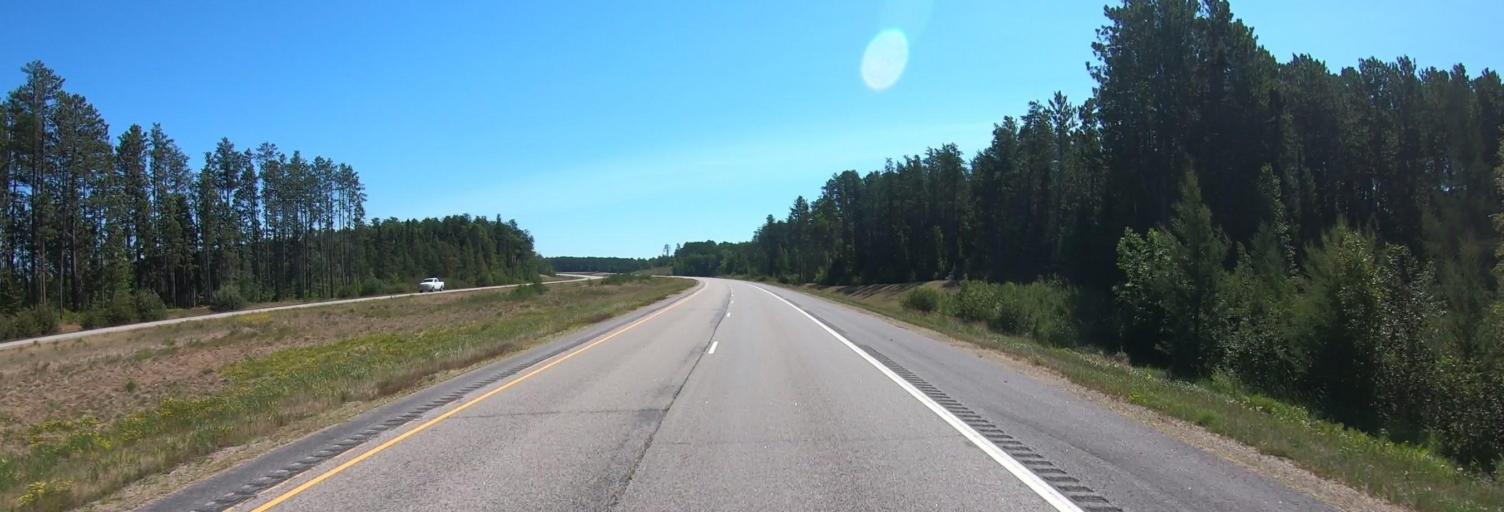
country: US
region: Minnesota
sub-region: Saint Louis County
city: Mountain Iron
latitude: 47.6603
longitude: -92.6207
